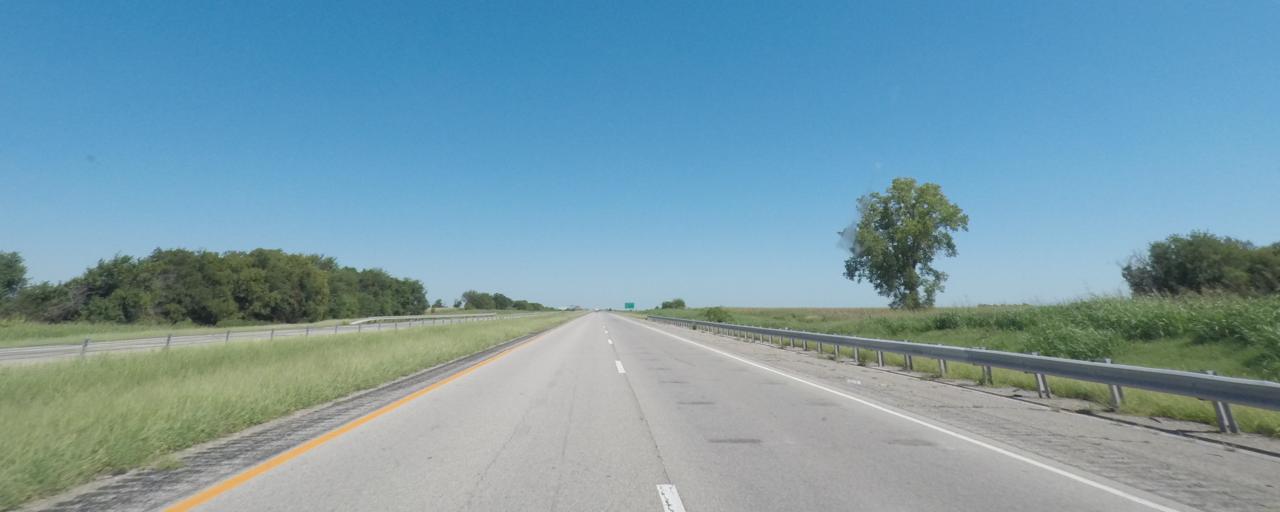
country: US
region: Oklahoma
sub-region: Kay County
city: Tonkawa
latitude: 36.7264
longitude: -97.3457
